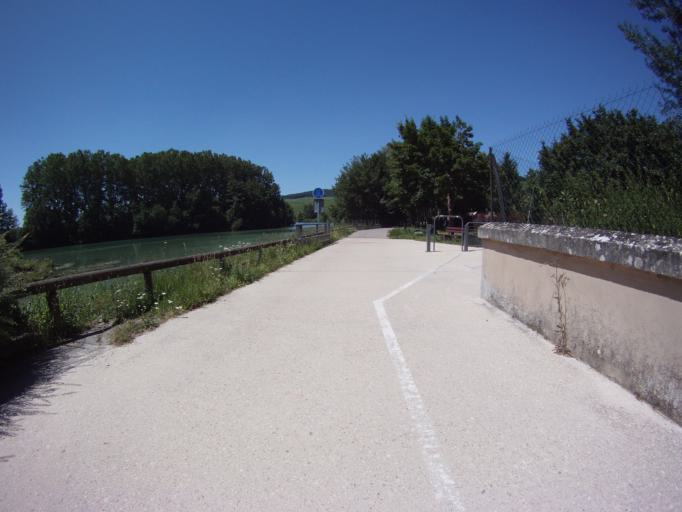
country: FR
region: Champagne-Ardenne
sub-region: Departement de la Marne
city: Epernay
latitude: 49.0706
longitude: 3.9440
